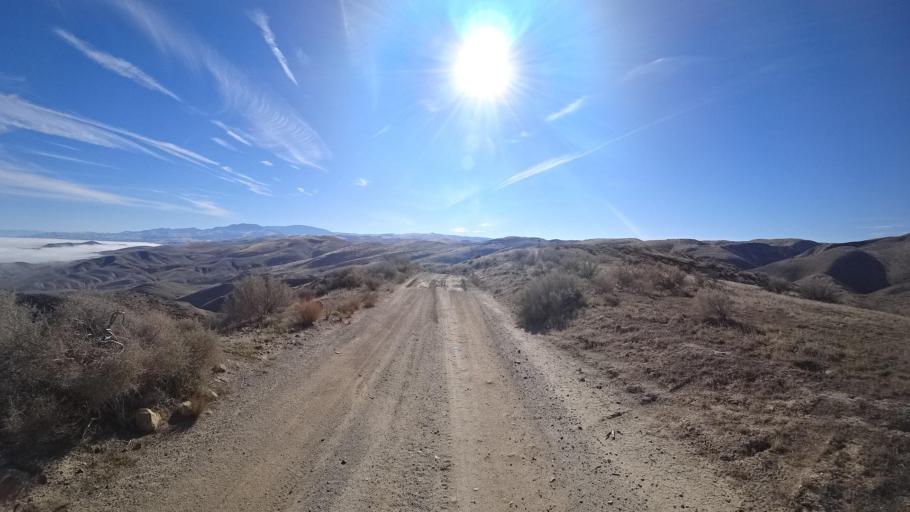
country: US
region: California
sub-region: Kern County
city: Maricopa
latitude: 35.0166
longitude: -119.4728
